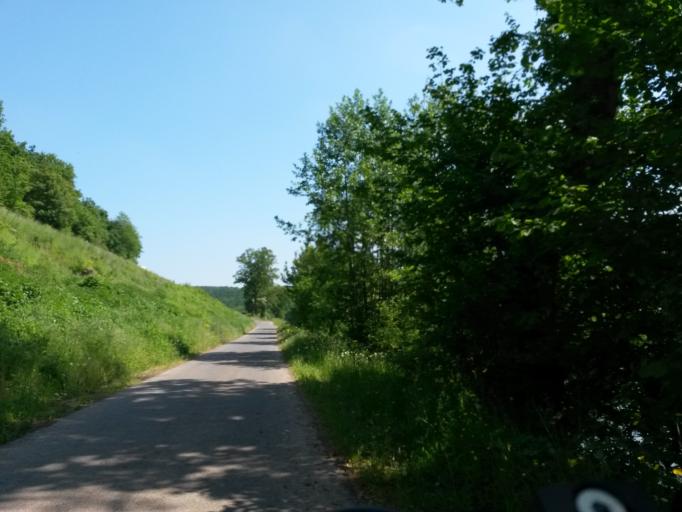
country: DE
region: Bavaria
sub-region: Regierungsbezirk Unterfranken
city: Euerdorf
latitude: 50.1541
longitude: 10.0176
